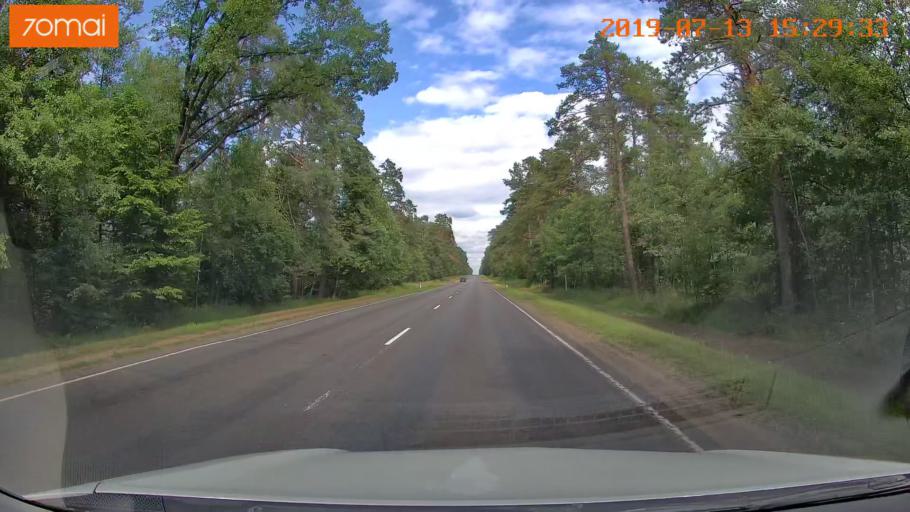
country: BY
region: Mogilev
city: Babruysk
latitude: 53.1074
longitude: 29.0674
